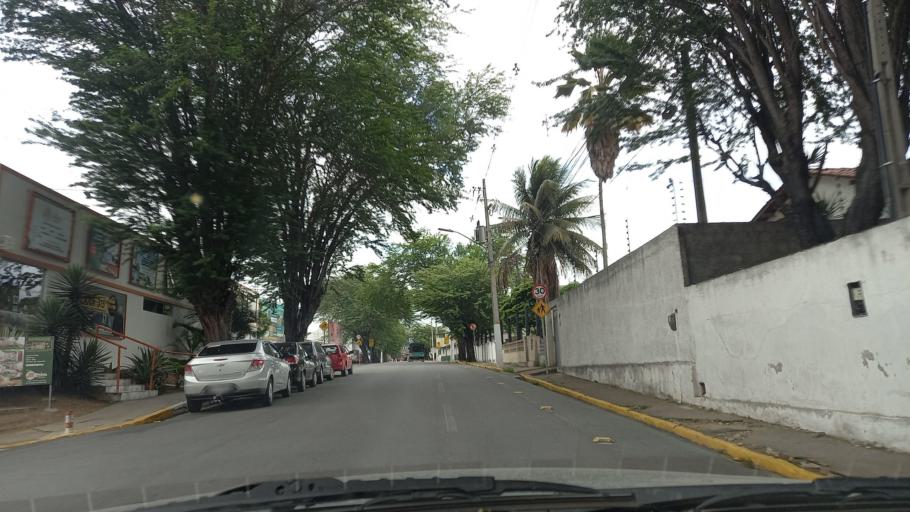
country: BR
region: Pernambuco
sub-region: Caruaru
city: Caruaru
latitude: -8.2810
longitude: -35.9678
